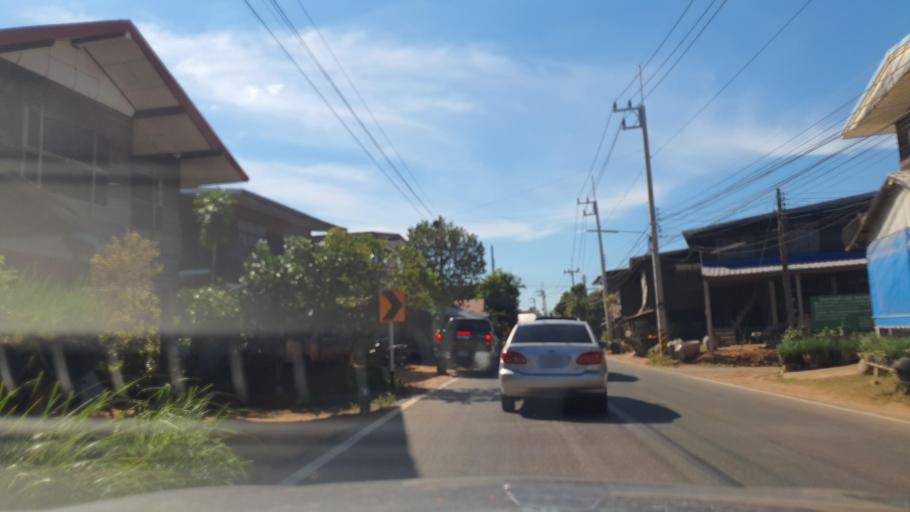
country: TH
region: Kalasin
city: Khao Wong
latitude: 16.7379
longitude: 104.1027
